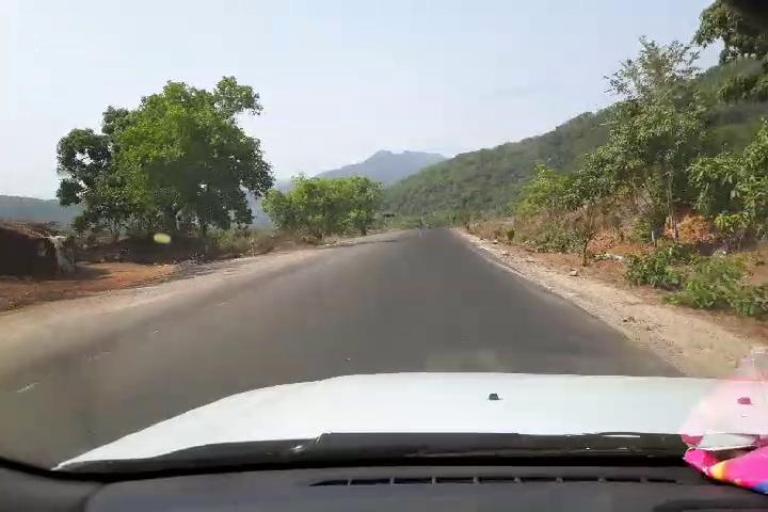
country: SL
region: Western Area
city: Hastings
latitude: 8.2756
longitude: -13.1567
